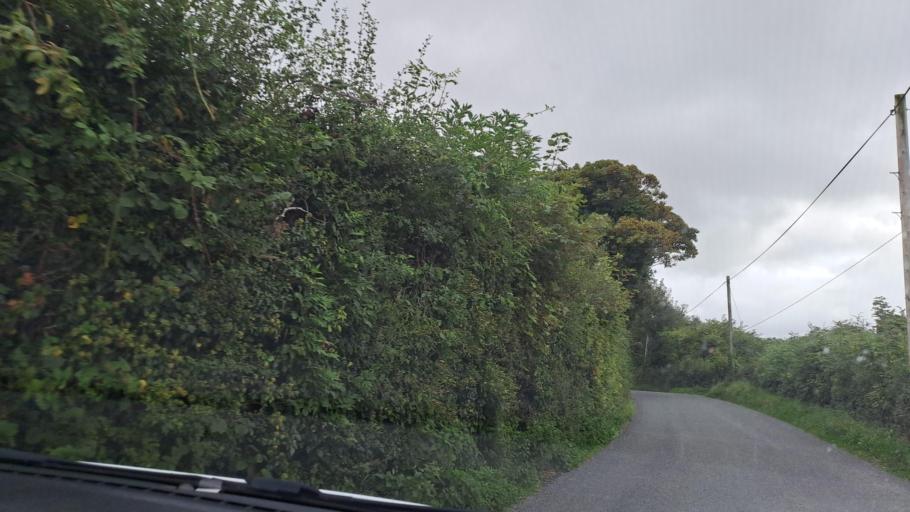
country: IE
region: Ulster
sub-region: County Monaghan
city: Carrickmacross
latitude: 54.0212
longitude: -6.7234
